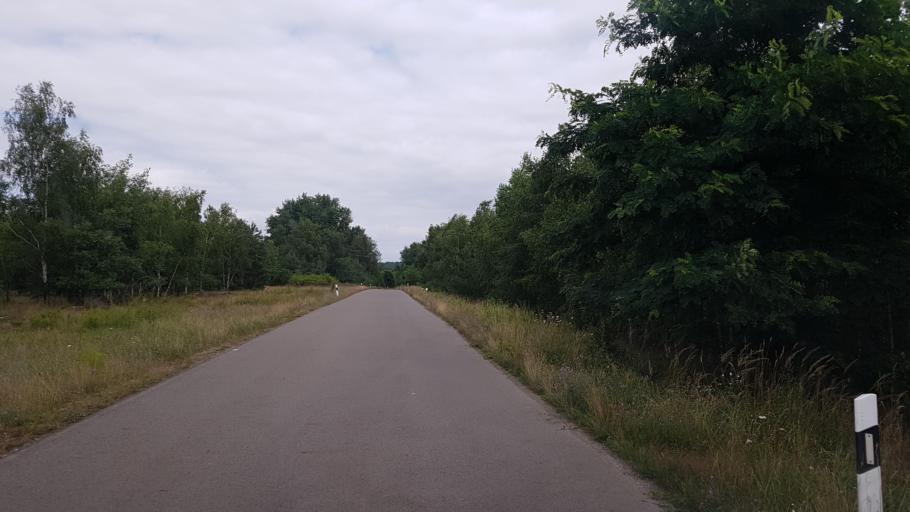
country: DE
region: Brandenburg
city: Altdobern
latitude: 51.6422
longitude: 14.0872
